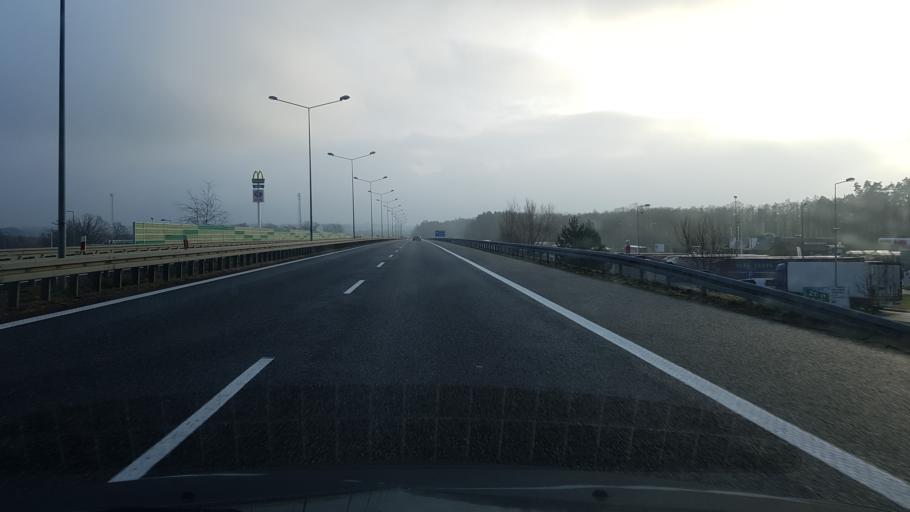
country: PL
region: Silesian Voivodeship
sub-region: Powiat gliwicki
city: Sosnicowice
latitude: 50.3127
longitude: 18.5498
